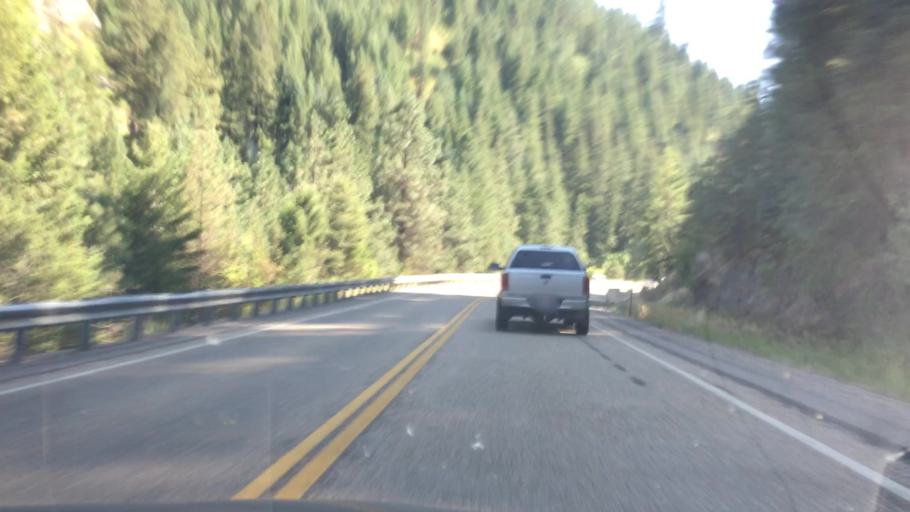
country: US
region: Idaho
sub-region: Valley County
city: Cascade
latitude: 44.1459
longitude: -116.1133
